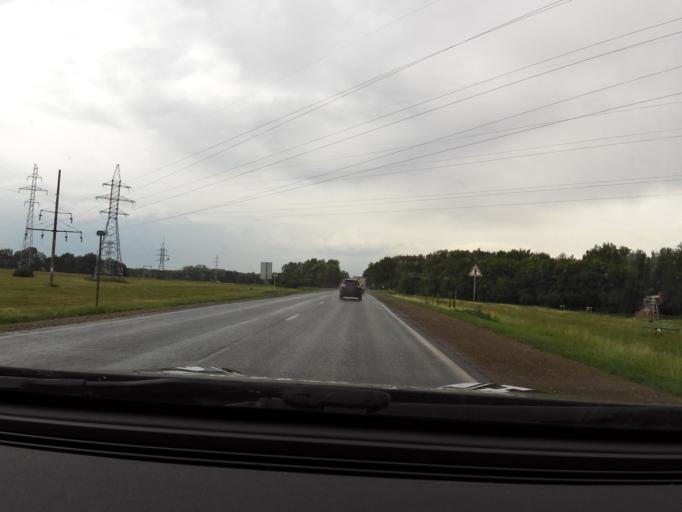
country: RU
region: Bashkortostan
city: Mikhaylovka
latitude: 54.8360
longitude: 55.8039
